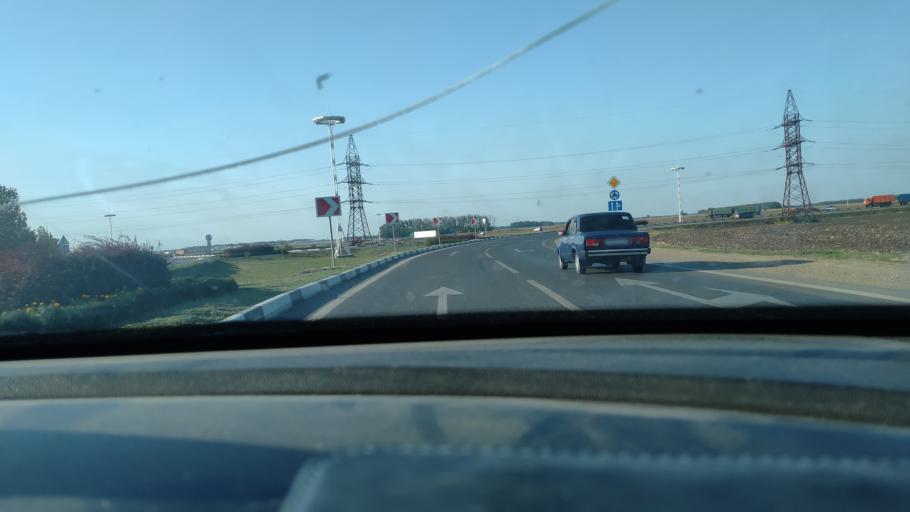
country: RU
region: Krasnodarskiy
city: Timashevsk
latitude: 45.6251
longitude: 38.9861
